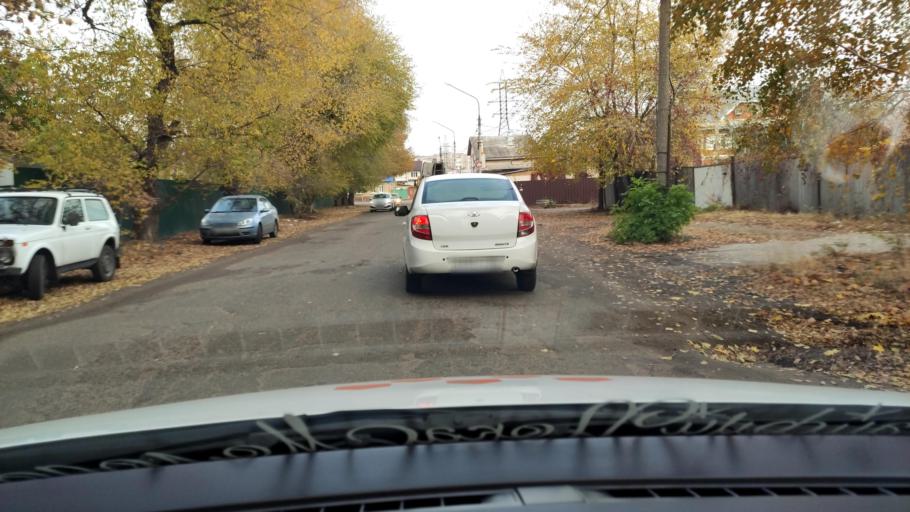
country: RU
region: Voronezj
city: Voronezh
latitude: 51.6637
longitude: 39.1677
